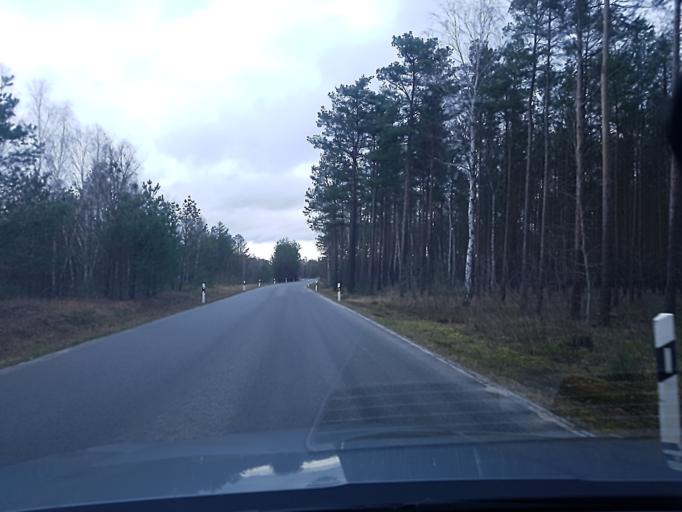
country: DE
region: Brandenburg
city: Schonewalde
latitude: 51.6326
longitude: 13.6351
